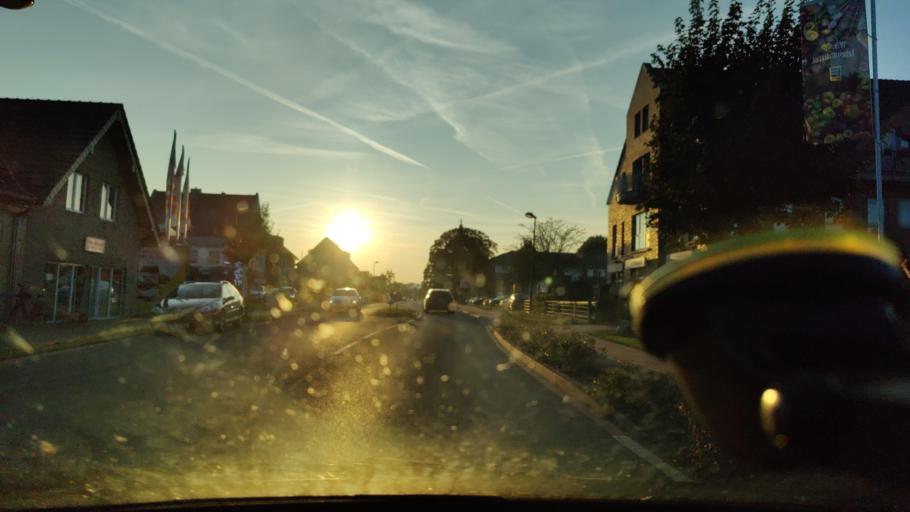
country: DE
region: North Rhine-Westphalia
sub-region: Regierungsbezirk Dusseldorf
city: Mehrhoog
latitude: 51.7390
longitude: 6.5129
